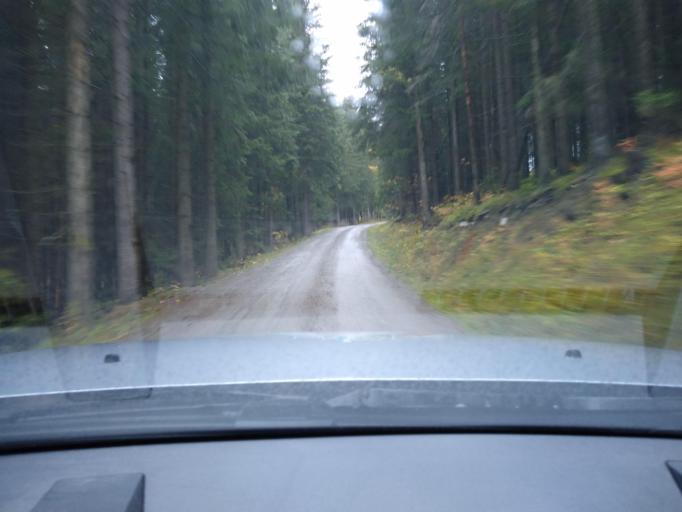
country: NO
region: Oppland
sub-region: Ringebu
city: Ringebu
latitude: 61.5509
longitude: 10.1493
